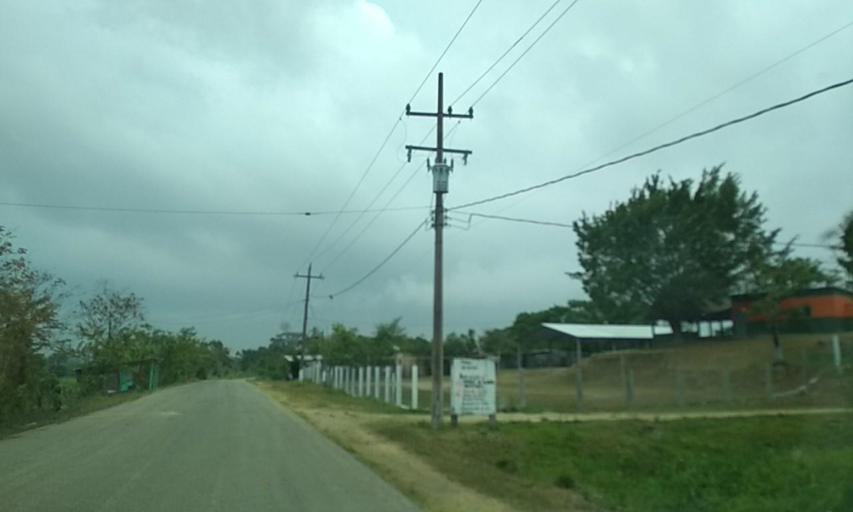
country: MX
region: Tabasco
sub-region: Huimanguillo
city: Francisco Rueda
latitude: 17.5903
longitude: -94.0918
